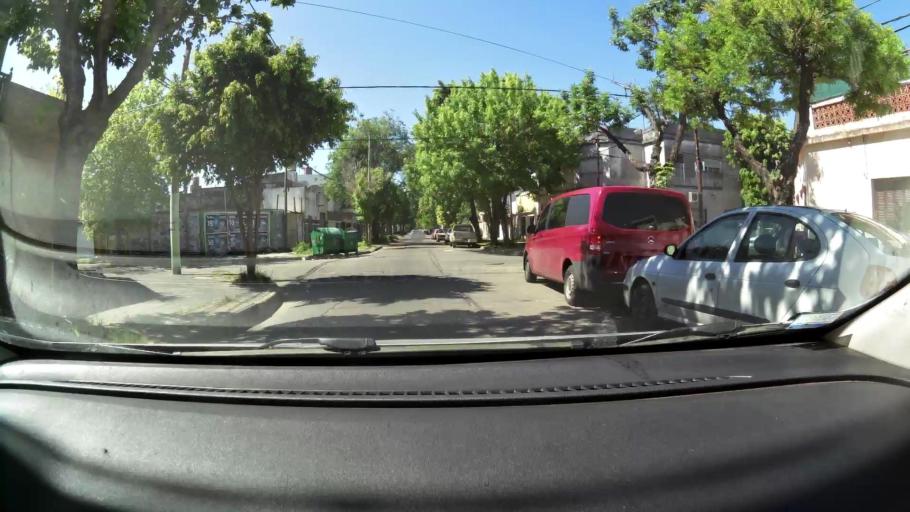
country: AR
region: Santa Fe
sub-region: Departamento de Rosario
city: Rosario
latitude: -32.9424
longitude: -60.6871
